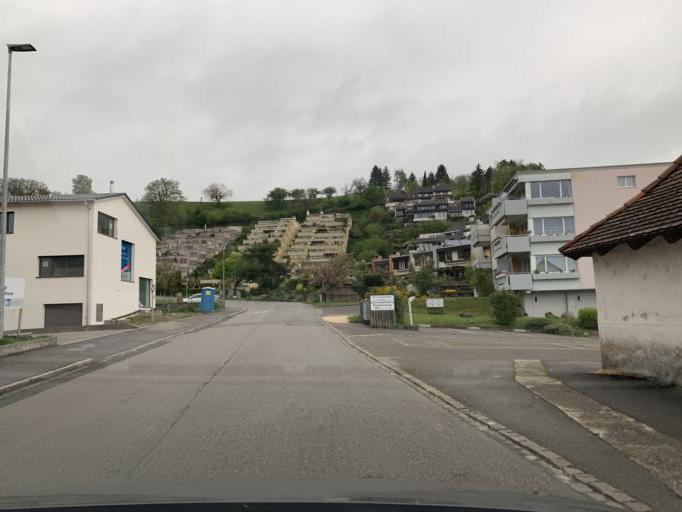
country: CH
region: Schaffhausen
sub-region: Bezirk Schaffhausen
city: Schaffhausen
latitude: 47.7067
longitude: 8.6183
